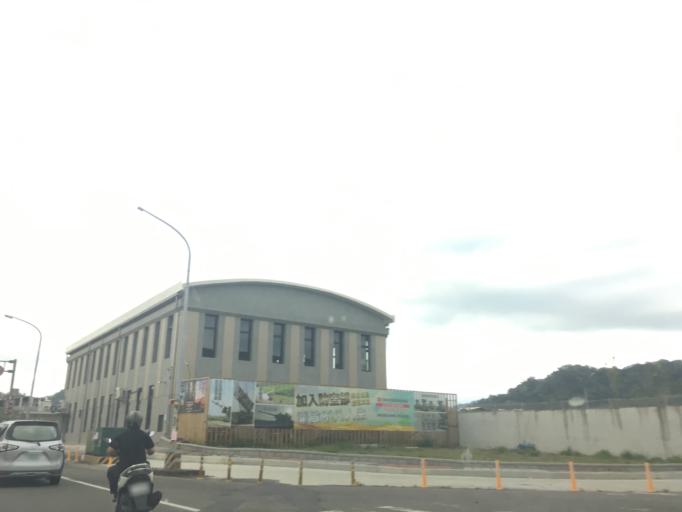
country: TW
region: Taiwan
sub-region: Taichung City
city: Taichung
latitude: 24.1505
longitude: 120.7331
